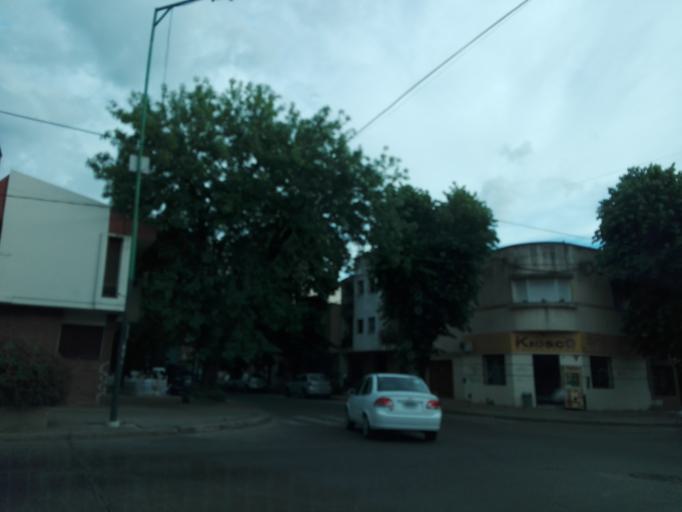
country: AR
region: Buenos Aires
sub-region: Partido de La Plata
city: La Plata
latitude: -34.9276
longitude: -57.9348
